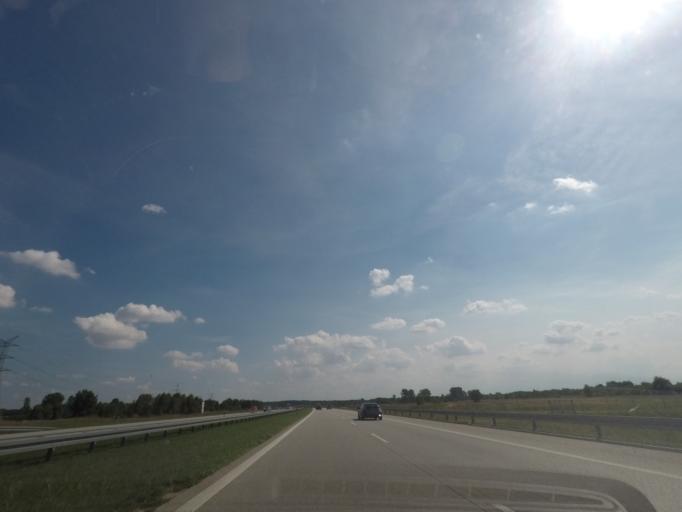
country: PL
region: Lodz Voivodeship
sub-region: Powiat lodzki wschodni
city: Tuszyn
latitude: 51.6227
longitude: 19.5685
